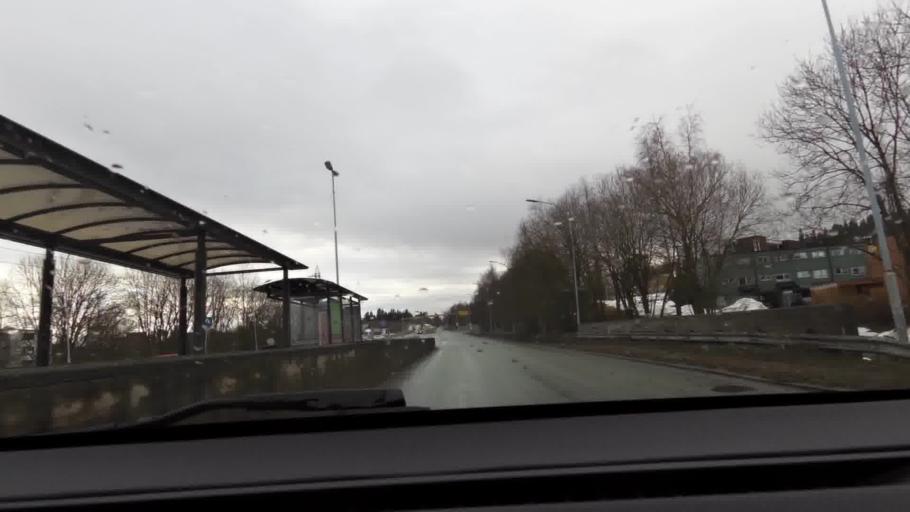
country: NO
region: Sor-Trondelag
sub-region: Trondheim
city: Trondheim
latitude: 63.3671
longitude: 10.3444
